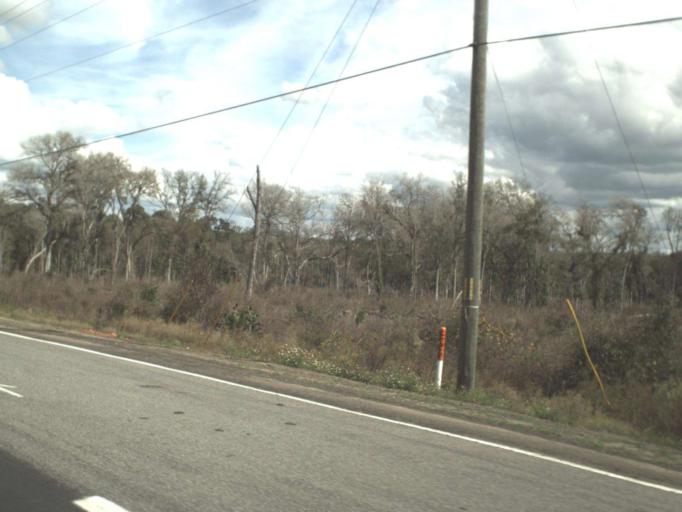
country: US
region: Florida
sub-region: Gadsden County
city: Havana
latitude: 30.5883
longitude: -84.4868
